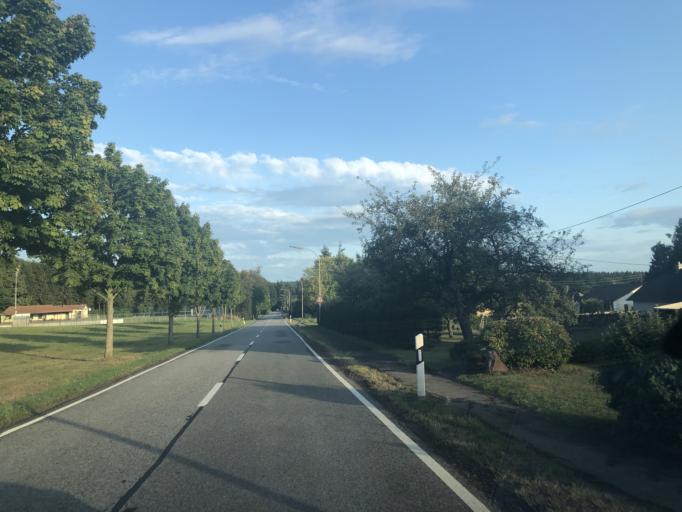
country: DE
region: Saarland
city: Nonnweiler
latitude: 49.6020
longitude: 6.9229
